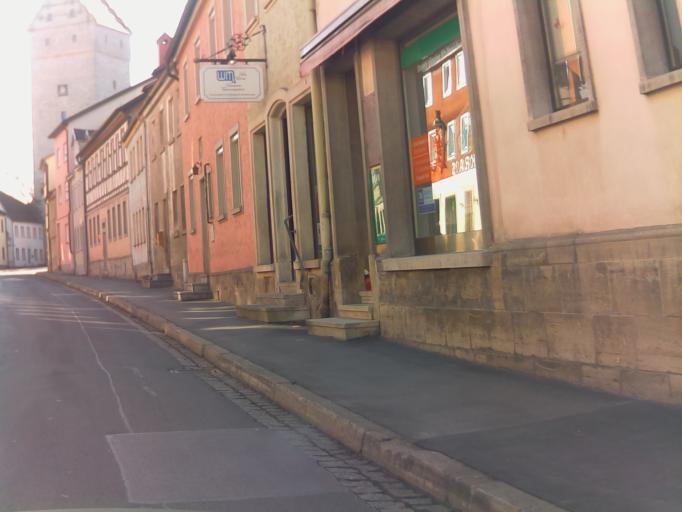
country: DE
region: Bavaria
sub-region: Regierungsbezirk Unterfranken
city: Munnerstadt
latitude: 50.2480
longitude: 10.1943
